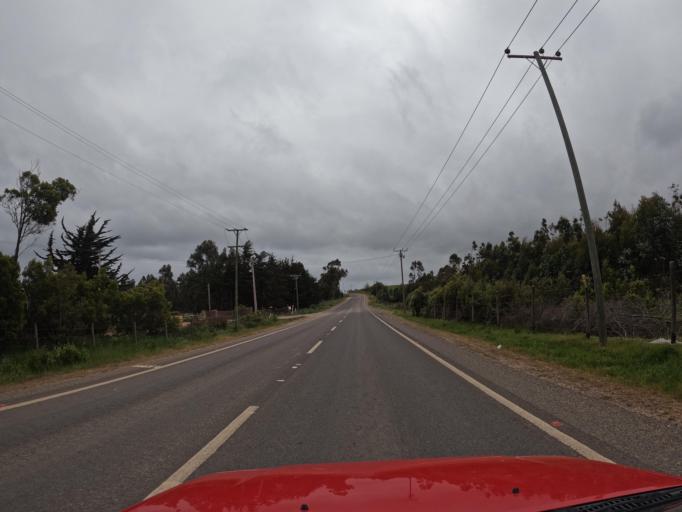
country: CL
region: O'Higgins
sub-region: Provincia de Colchagua
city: Santa Cruz
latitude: -34.4987
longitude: -72.0106
